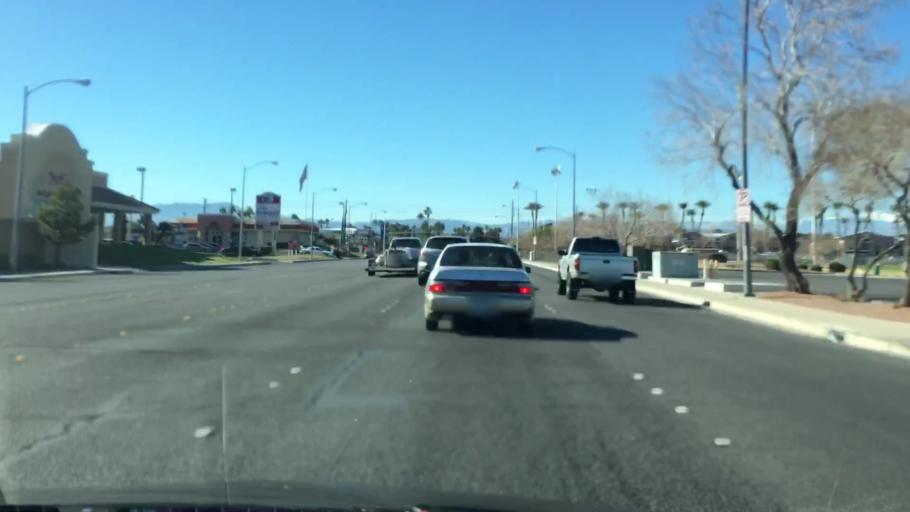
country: US
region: Nevada
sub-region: Clark County
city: Whitney
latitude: 36.0570
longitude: -115.1156
